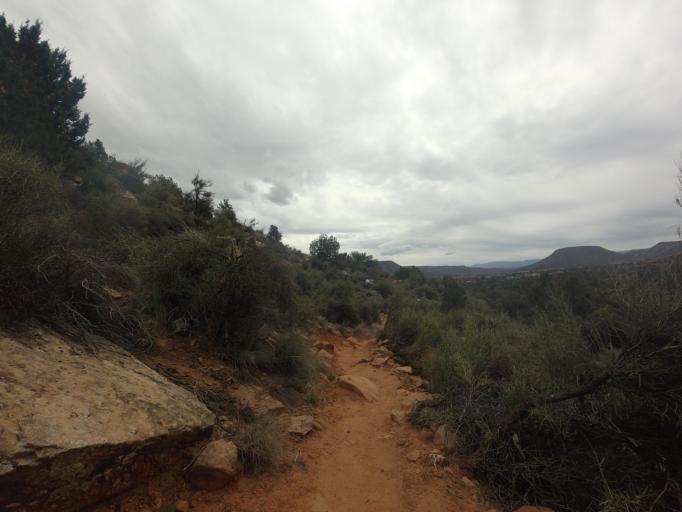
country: US
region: Arizona
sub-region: Yavapai County
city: Village of Oak Creek (Big Park)
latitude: 34.8010
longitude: -111.7606
